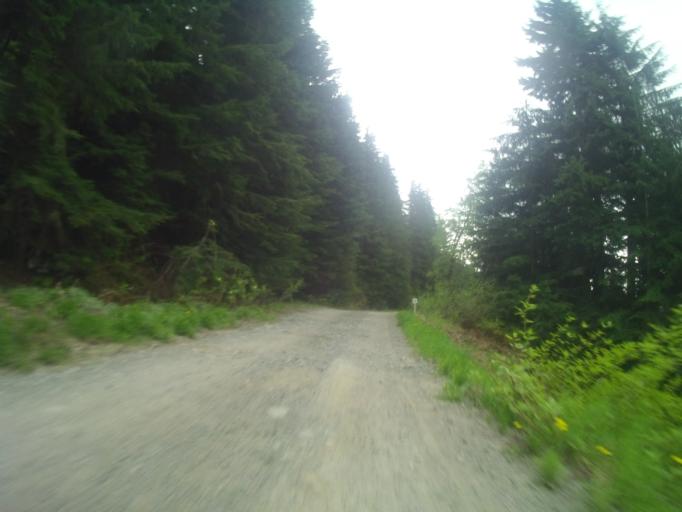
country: CA
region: British Columbia
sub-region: Fraser Valley Regional District
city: North Vancouver
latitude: 49.3795
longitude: -123.0641
